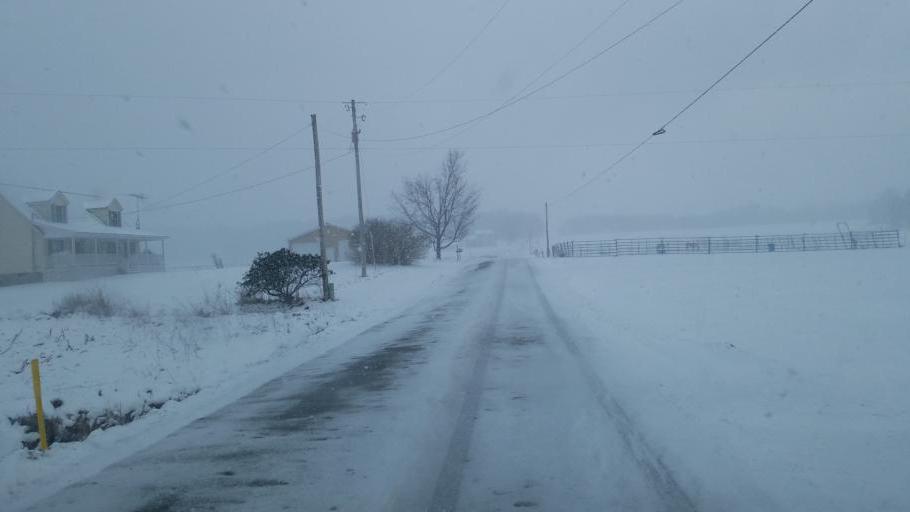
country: US
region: Pennsylvania
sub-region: Crawford County
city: Cochranton
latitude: 41.4405
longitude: -80.0123
